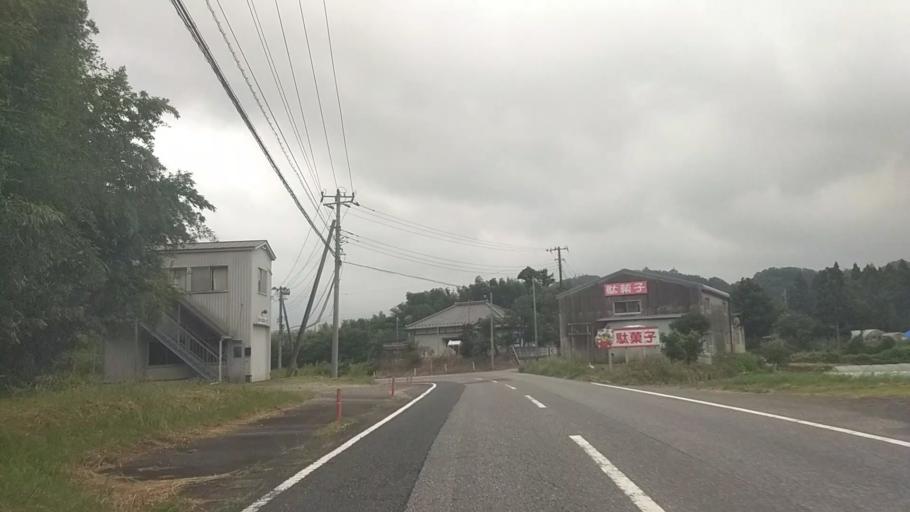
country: JP
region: Chiba
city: Kawaguchi
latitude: 35.2241
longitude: 140.0168
